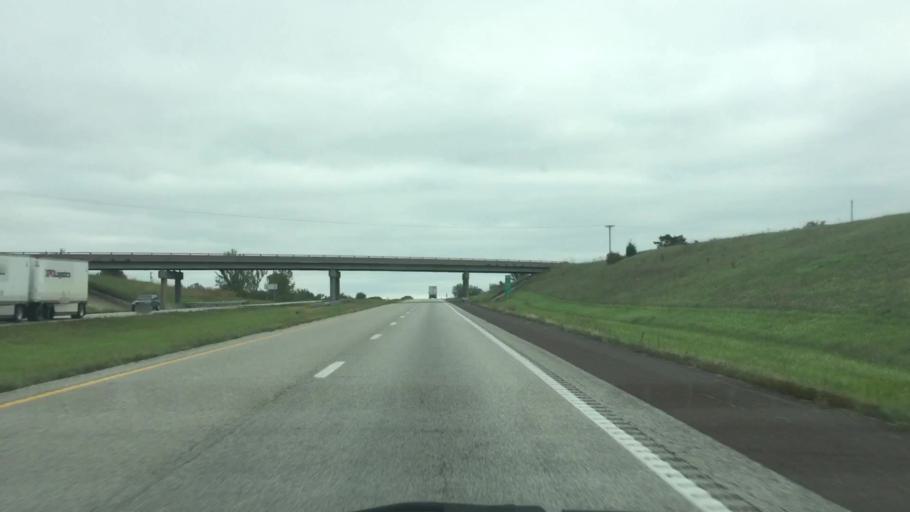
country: US
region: Missouri
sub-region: Daviess County
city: Gallatin
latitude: 39.9307
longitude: -94.1315
